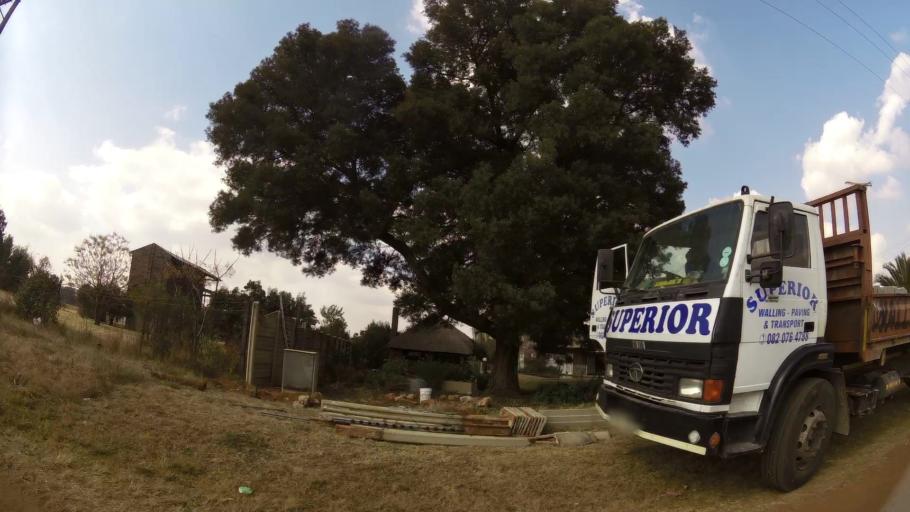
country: ZA
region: Mpumalanga
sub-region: Nkangala District Municipality
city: Delmas
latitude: -26.1521
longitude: 28.5481
